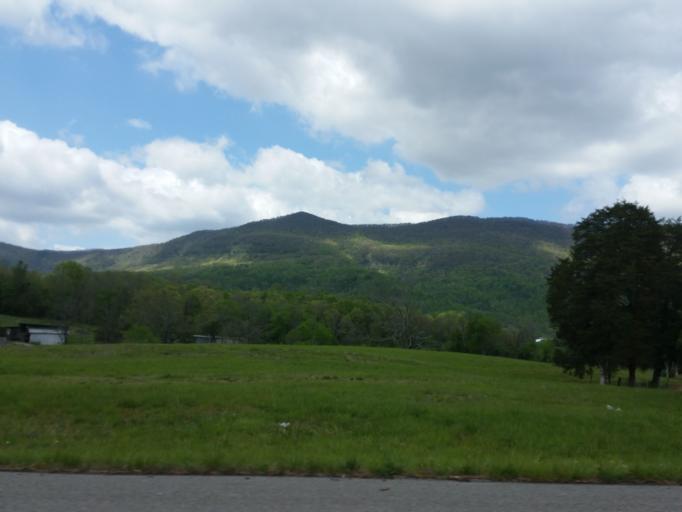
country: US
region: Tennessee
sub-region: Campbell County
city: Fincastle
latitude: 36.4459
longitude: -83.9504
